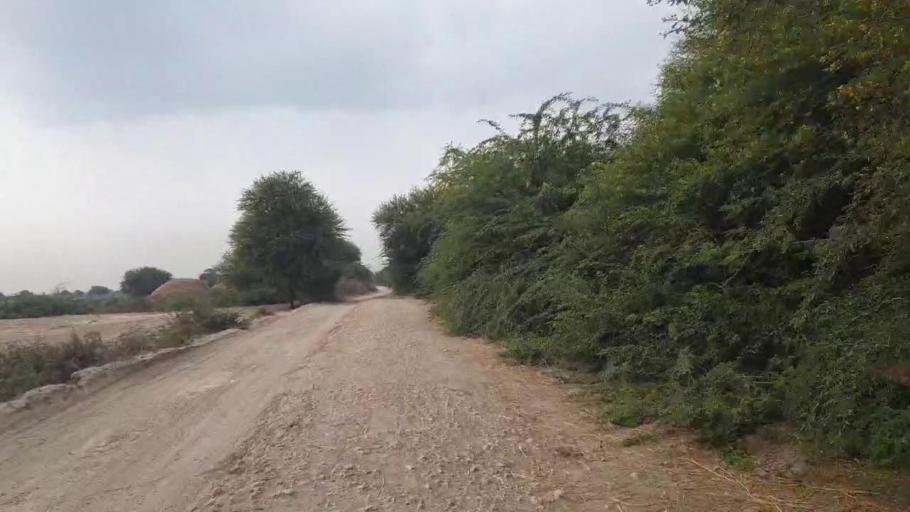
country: PK
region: Sindh
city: Talhar
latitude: 24.9167
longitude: 68.7761
